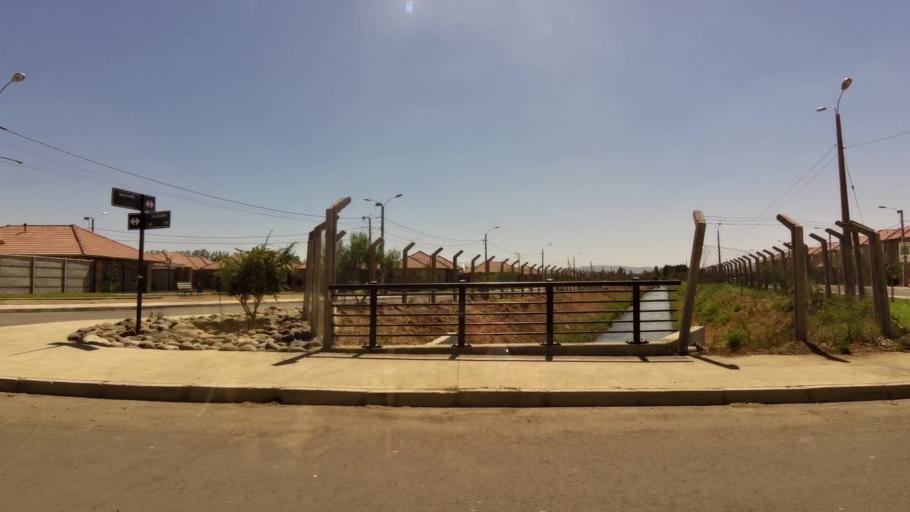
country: CL
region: Maule
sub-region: Provincia de Talca
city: Talca
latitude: -35.4348
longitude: -71.5923
